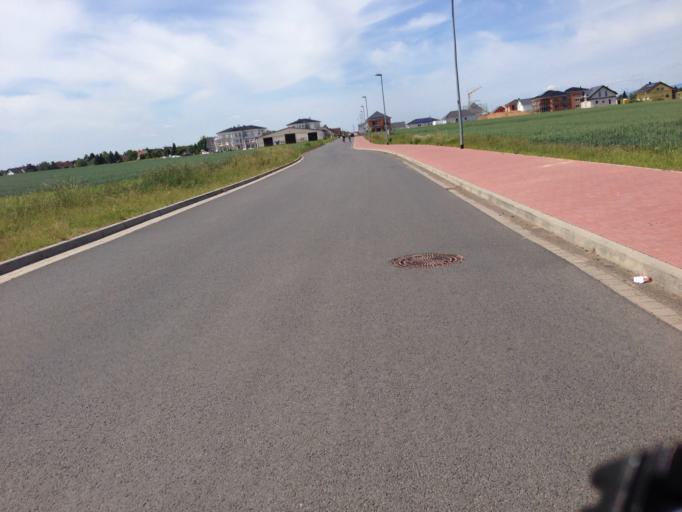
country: DE
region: Hesse
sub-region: Regierungsbezirk Darmstadt
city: Erlensee
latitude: 50.1743
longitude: 9.0004
